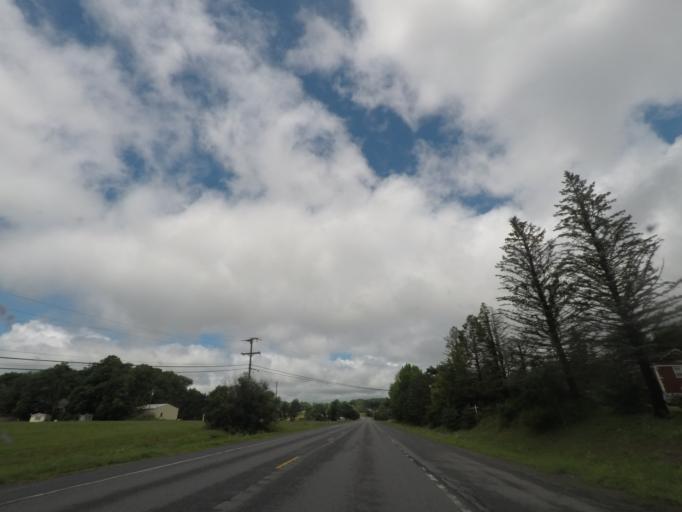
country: US
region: Massachusetts
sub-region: Berkshire County
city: Lanesborough
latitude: 42.5924
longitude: -73.3686
